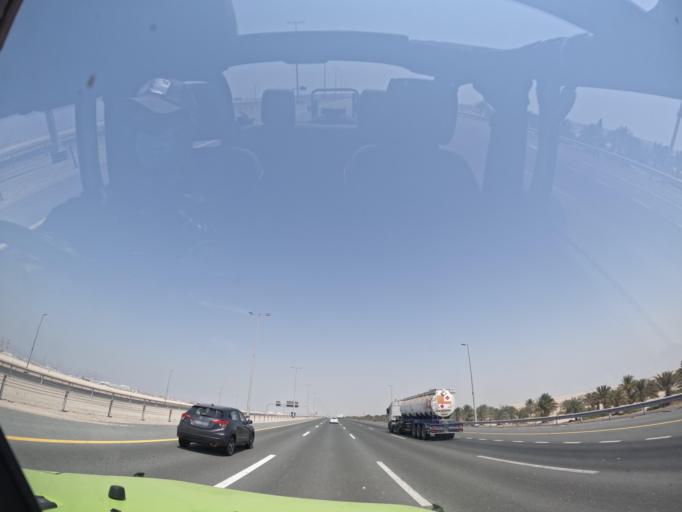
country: AE
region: Abu Dhabi
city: Abu Dhabi
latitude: 24.2541
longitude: 54.4814
